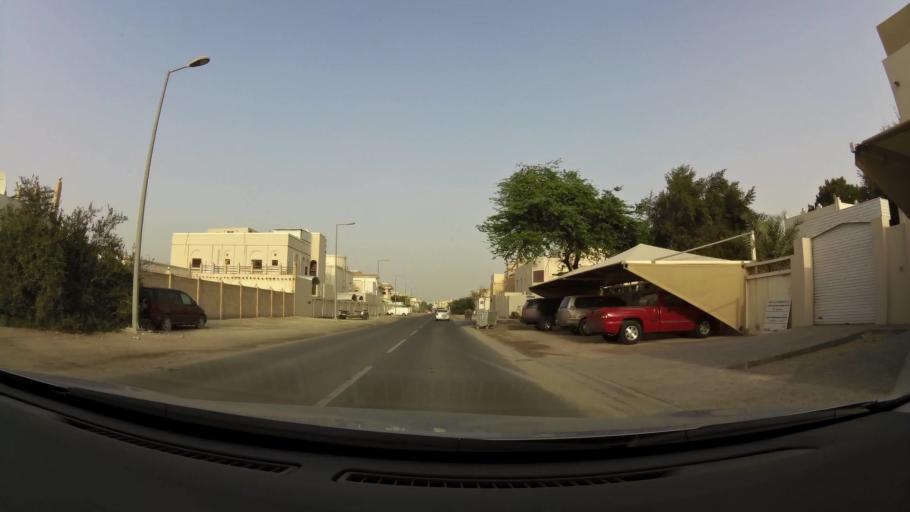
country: QA
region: Baladiyat ar Rayyan
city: Ar Rayyan
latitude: 25.2477
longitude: 51.4477
